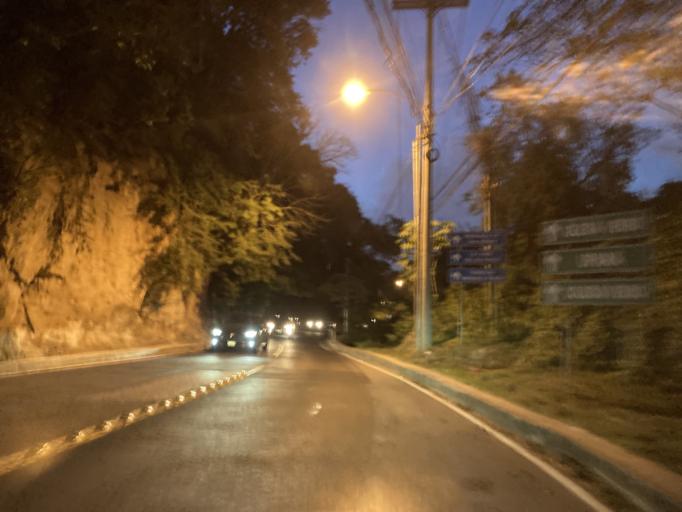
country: GT
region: Guatemala
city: Santa Catarina Pinula
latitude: 14.5990
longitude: -90.4665
